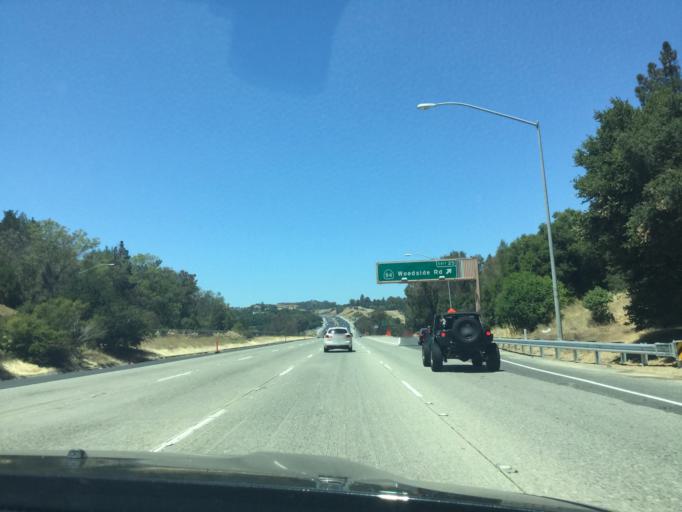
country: US
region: California
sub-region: San Mateo County
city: Woodside
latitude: 37.4319
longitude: -122.2388
